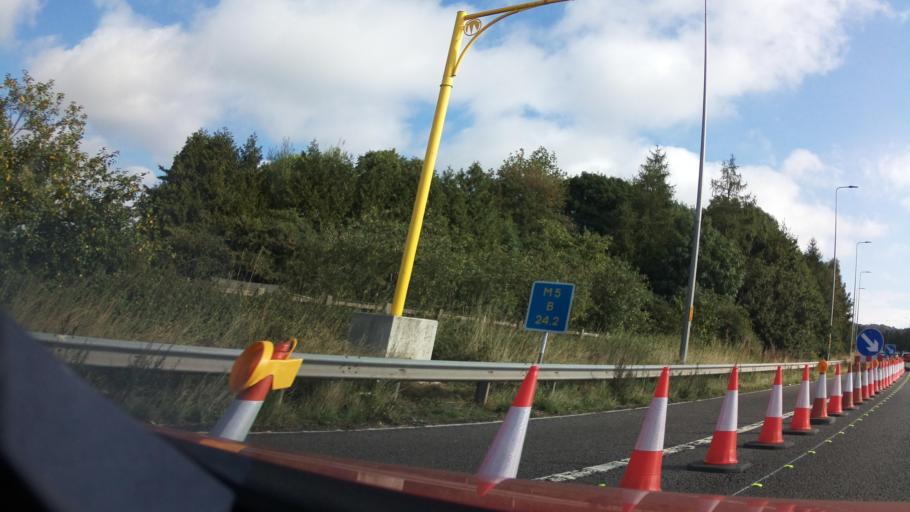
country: GB
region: England
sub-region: Worcestershire
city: Bromsgrove
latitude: 52.3708
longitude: -2.0570
